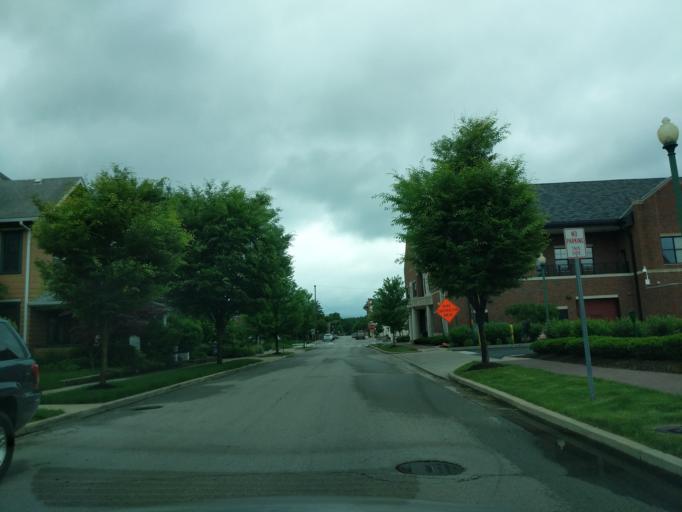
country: US
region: Indiana
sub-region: Hamilton County
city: Noblesville
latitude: 40.0447
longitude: -86.0112
